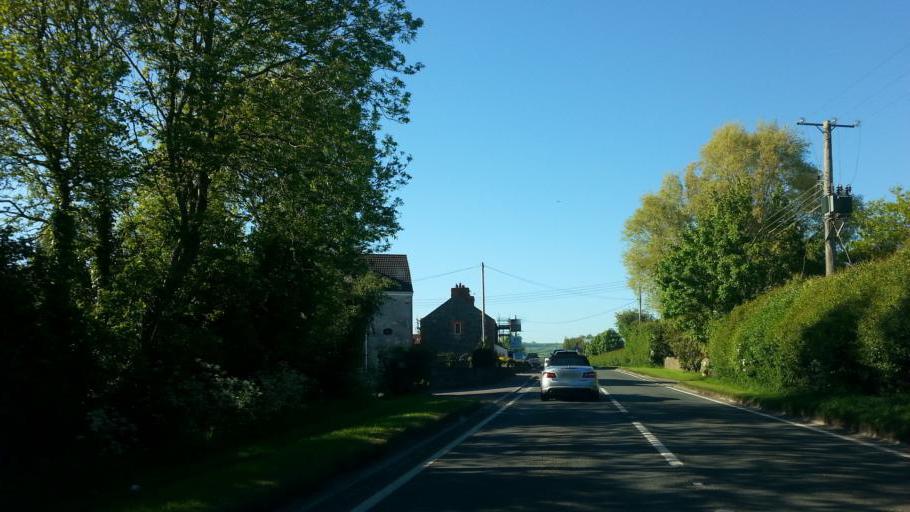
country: GB
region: England
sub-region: Somerset
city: Evercreech
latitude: 51.1308
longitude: -2.5161
